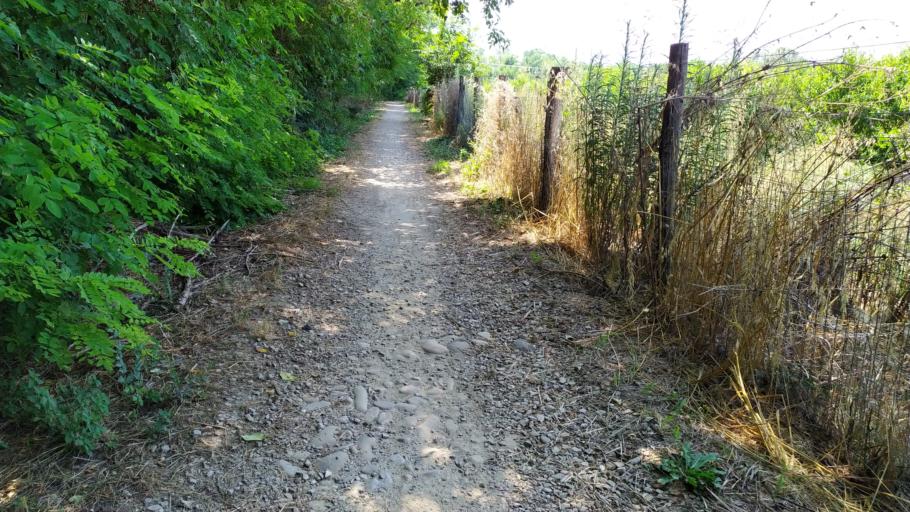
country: IT
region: Emilia-Romagna
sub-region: Forli-Cesena
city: Castrocaro Terme e Terra del Sole
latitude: 44.2021
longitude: 11.9976
